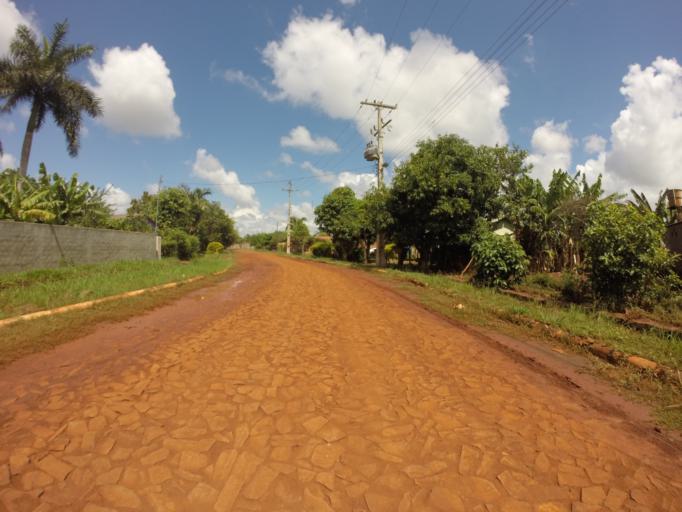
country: PY
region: Alto Parana
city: Ciudad del Este
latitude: -25.4009
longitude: -54.6364
